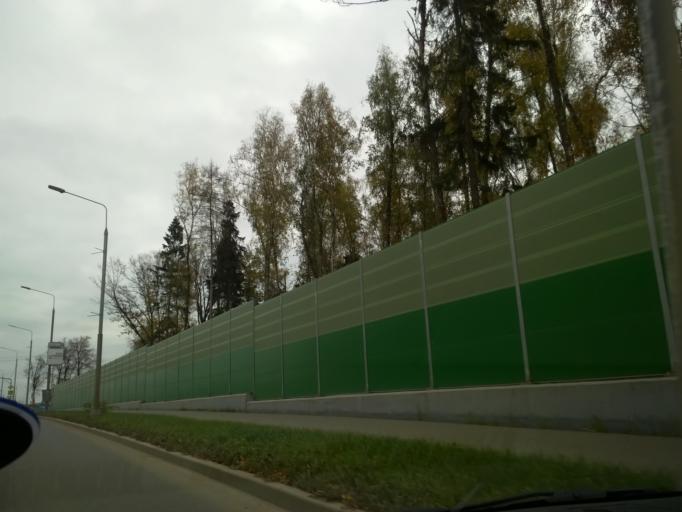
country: RU
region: Moskovskaya
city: Kommunarka
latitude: 55.5596
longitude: 37.4884
